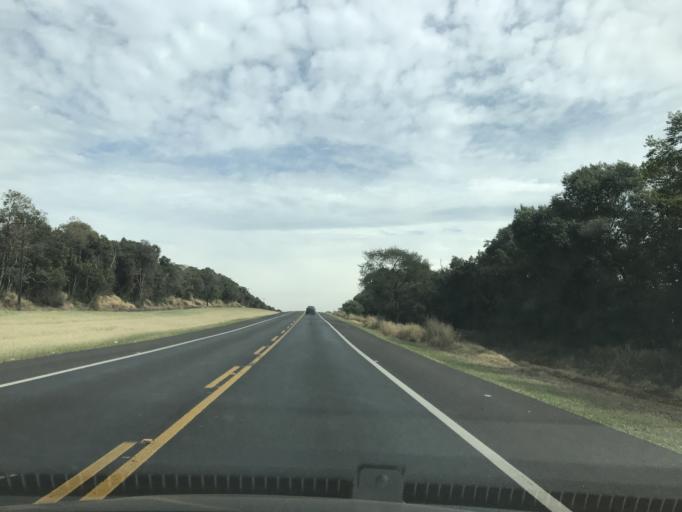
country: BR
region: Parana
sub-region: Cascavel
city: Cascavel
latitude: -25.0627
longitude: -53.6504
